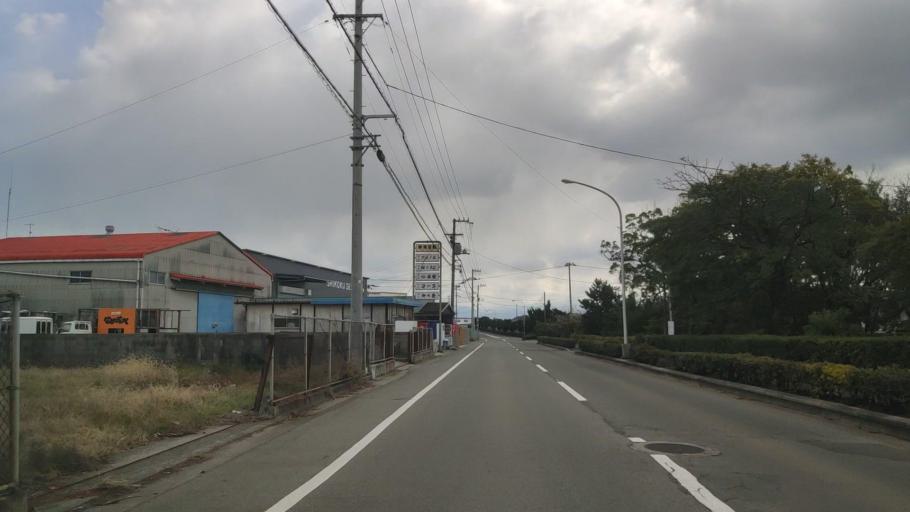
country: JP
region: Ehime
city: Saijo
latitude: 34.0542
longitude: 133.0221
